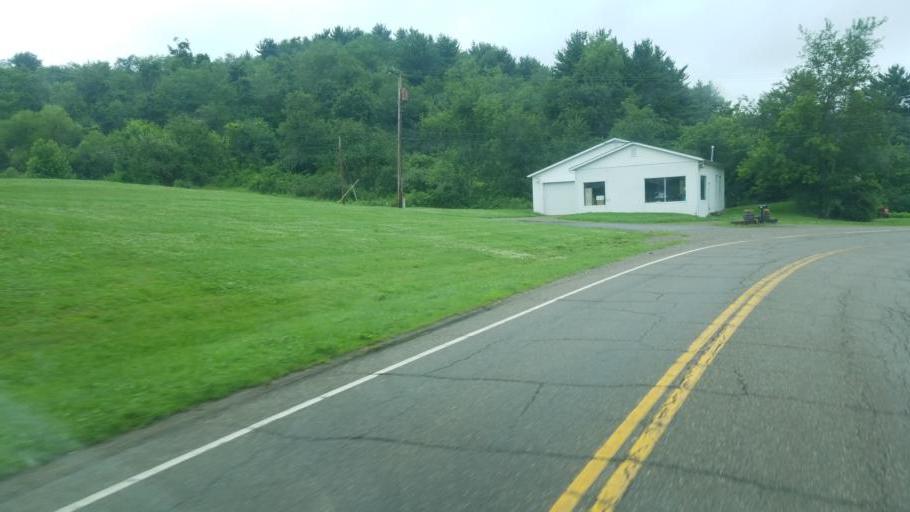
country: US
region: Ohio
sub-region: Columbiana County
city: Salineville
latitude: 40.5140
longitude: -80.8880
